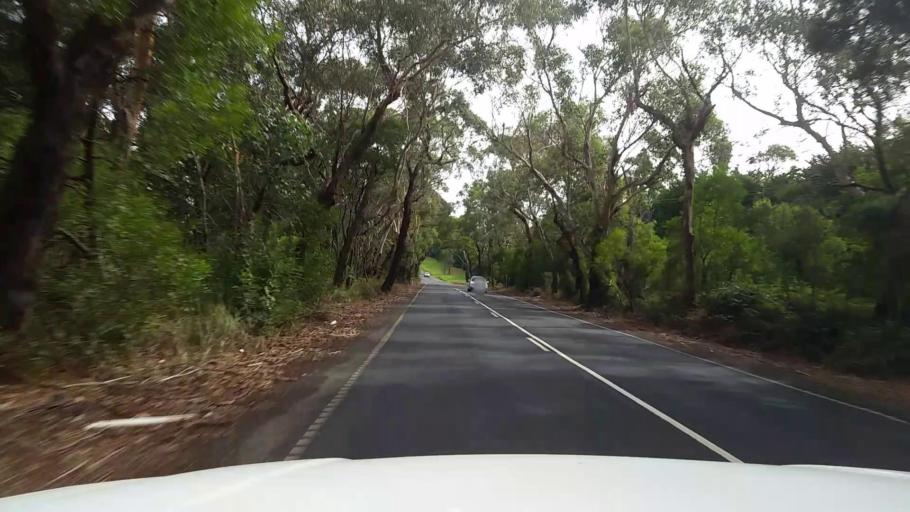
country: AU
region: Victoria
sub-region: Mornington Peninsula
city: Merricks
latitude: -38.3085
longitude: 145.0836
